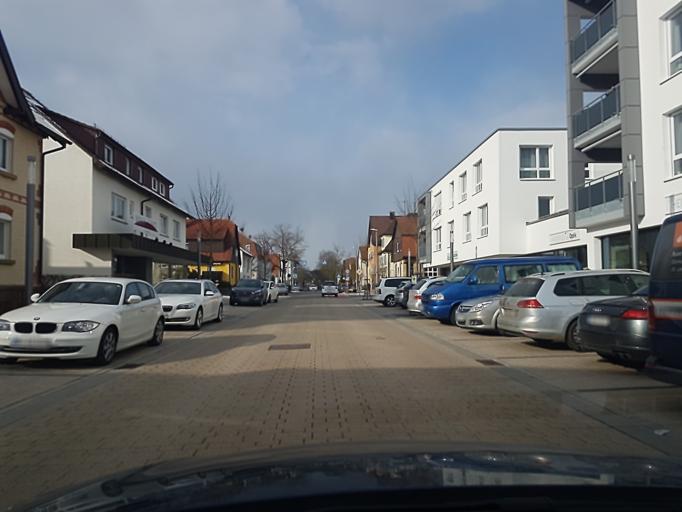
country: DE
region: Baden-Wuerttemberg
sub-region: Regierungsbezirk Stuttgart
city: Renningen
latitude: 48.7681
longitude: 8.9355
